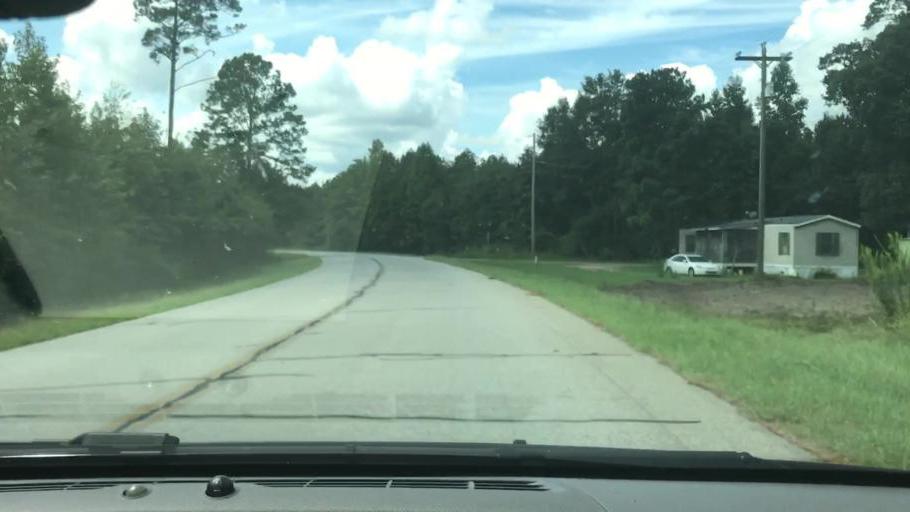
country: US
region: Georgia
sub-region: Stewart County
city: Lumpkin
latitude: 32.1436
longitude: -85.0168
